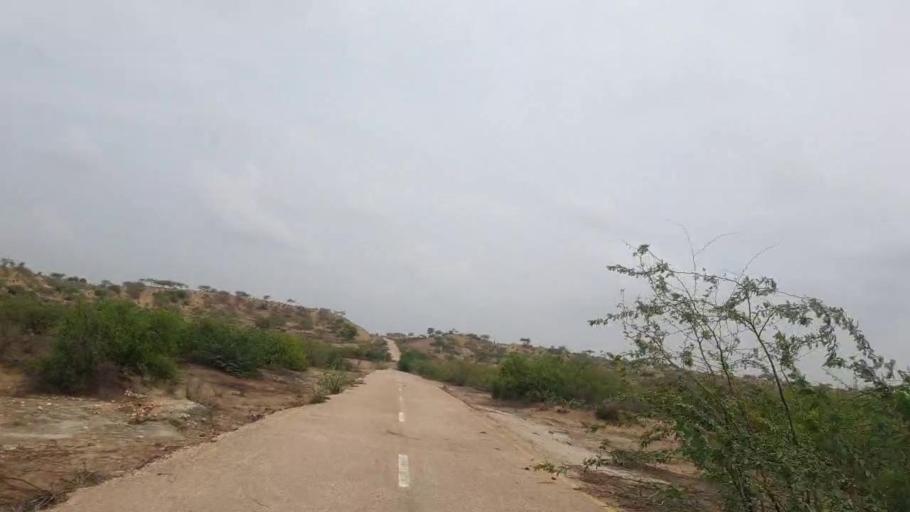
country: PK
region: Sindh
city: Naukot
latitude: 24.6283
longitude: 69.3563
